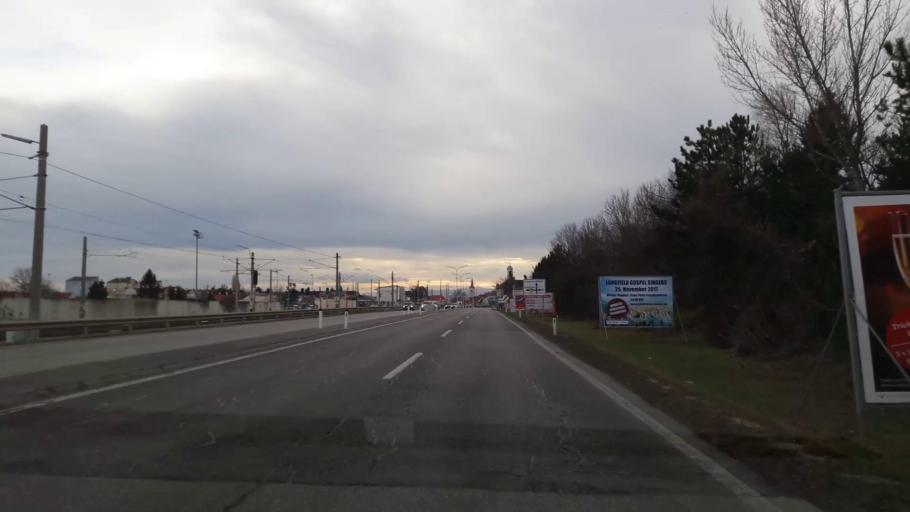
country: AT
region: Lower Austria
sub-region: Politischer Bezirk Modling
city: Wiener Neudorf
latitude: 48.0901
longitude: 16.3140
